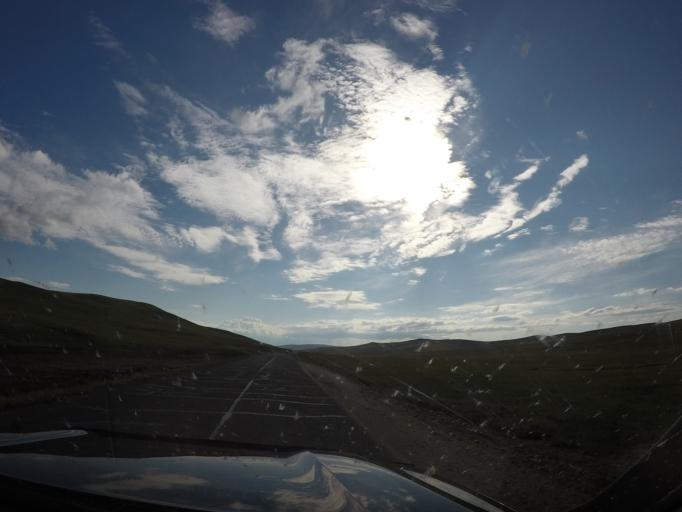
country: MN
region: Hentiy
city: Modot
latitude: 47.7937
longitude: 108.6852
